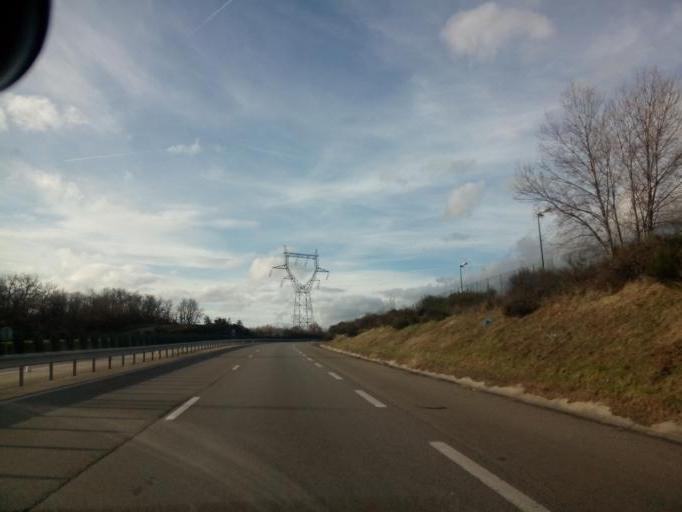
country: FR
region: Rhone-Alpes
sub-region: Departement de l'Ardeche
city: Felines
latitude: 45.3067
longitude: 4.7398
